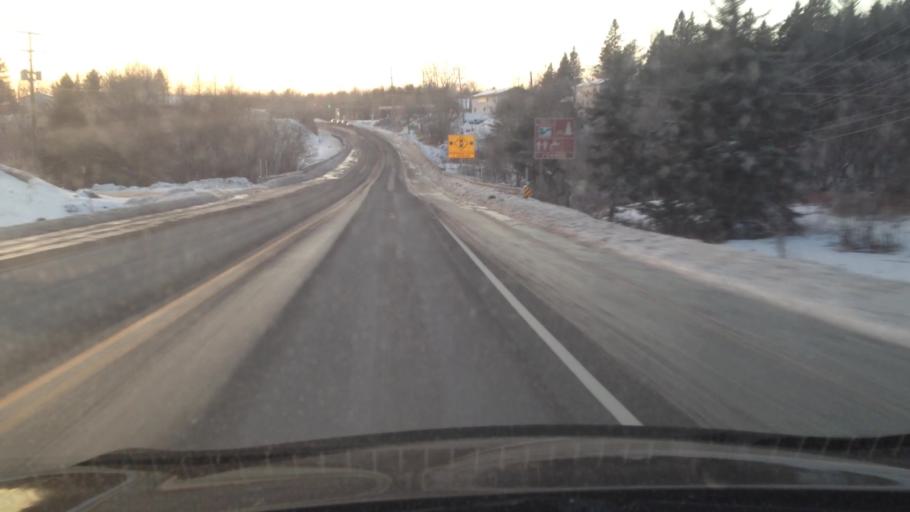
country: CA
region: Quebec
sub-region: Laurentides
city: Sainte-Sophie
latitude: 45.8324
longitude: -73.8771
